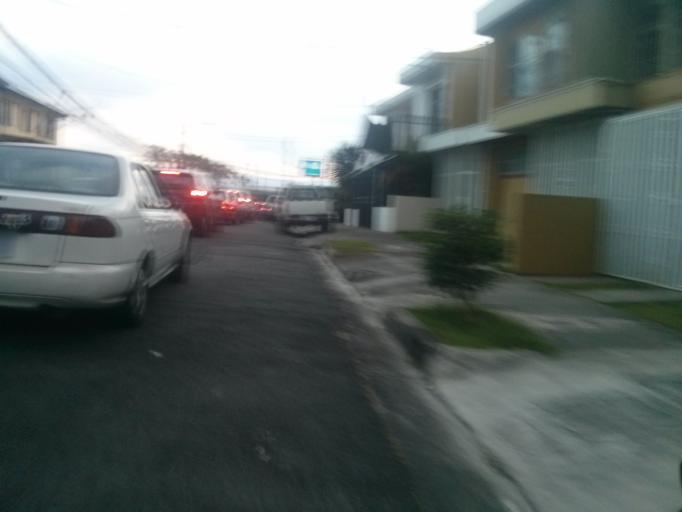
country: CR
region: San Jose
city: San Pedro
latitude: 9.9263
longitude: -84.0602
